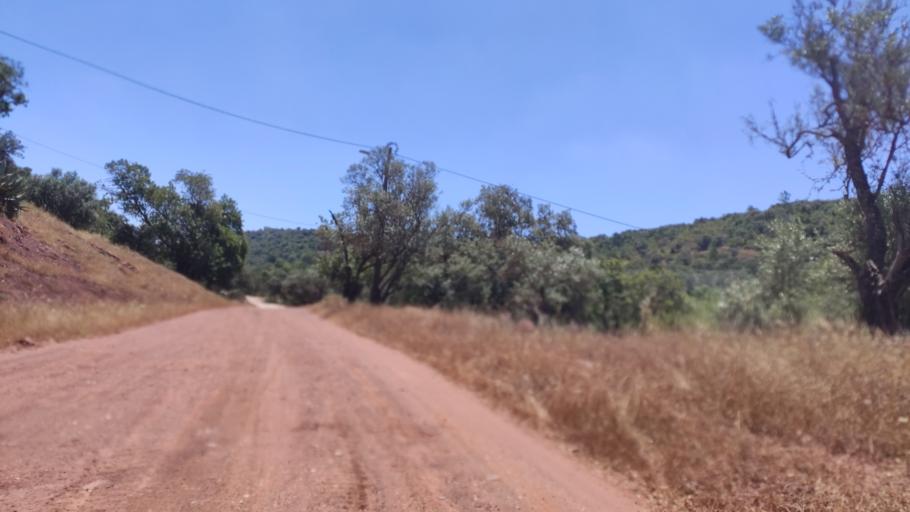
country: PT
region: Faro
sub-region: Sao Bras de Alportel
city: Sao Bras de Alportel
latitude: 37.1746
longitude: -7.9287
